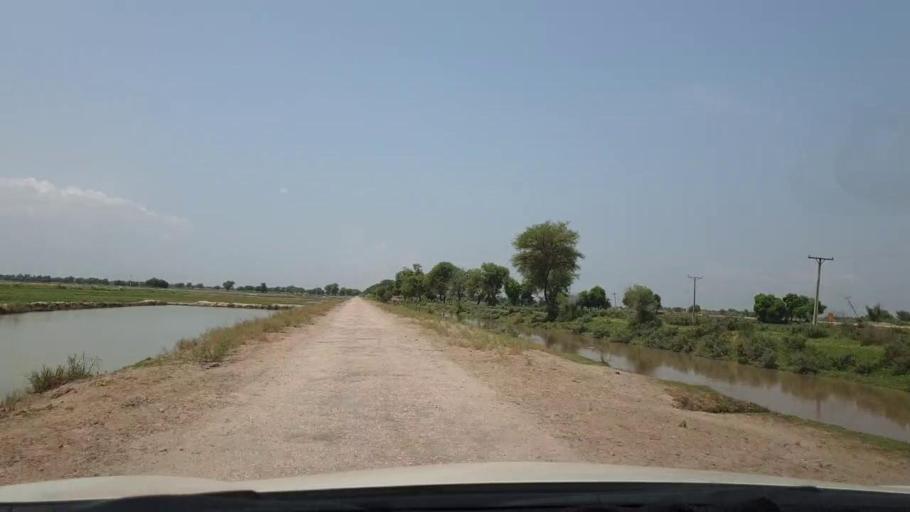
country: PK
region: Sindh
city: Ratodero
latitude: 27.8114
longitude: 68.2486
